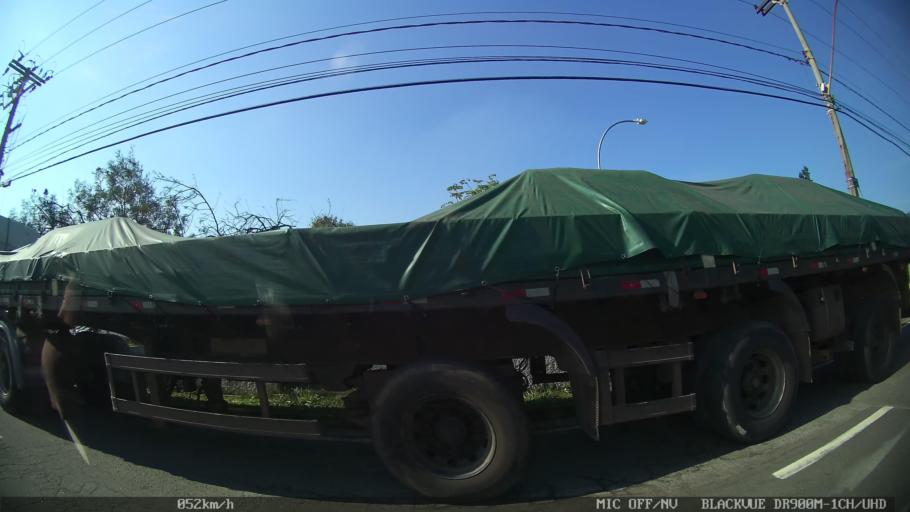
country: BR
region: Sao Paulo
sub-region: Campinas
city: Campinas
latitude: -22.9974
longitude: -47.1244
